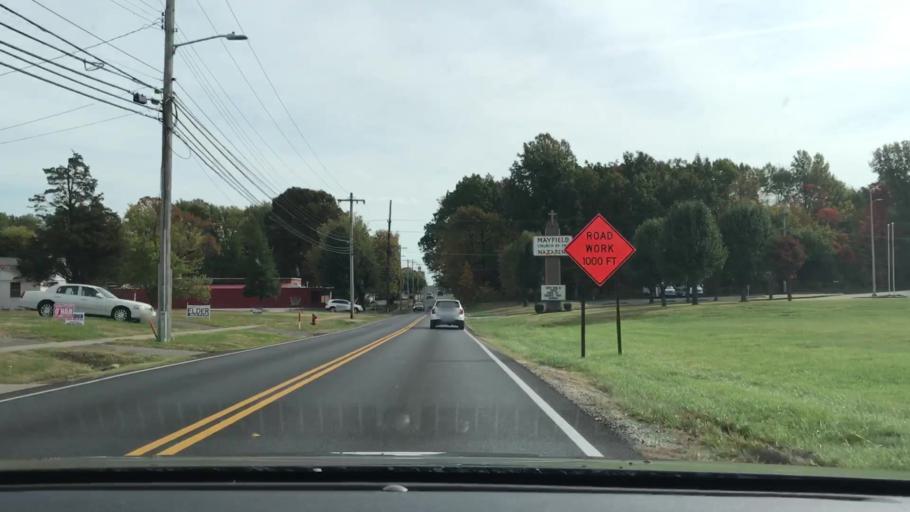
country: US
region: Kentucky
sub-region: Graves County
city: Mayfield
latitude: 36.7418
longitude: -88.6533
